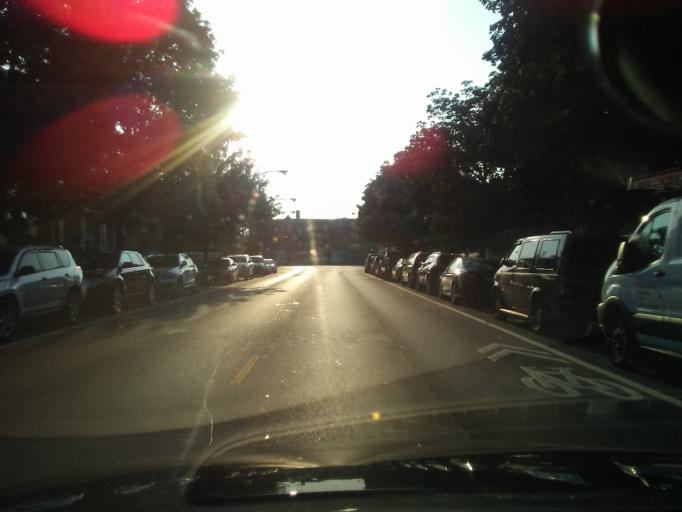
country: US
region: Illinois
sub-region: Cook County
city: Evanston
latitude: 42.0122
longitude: -87.6848
